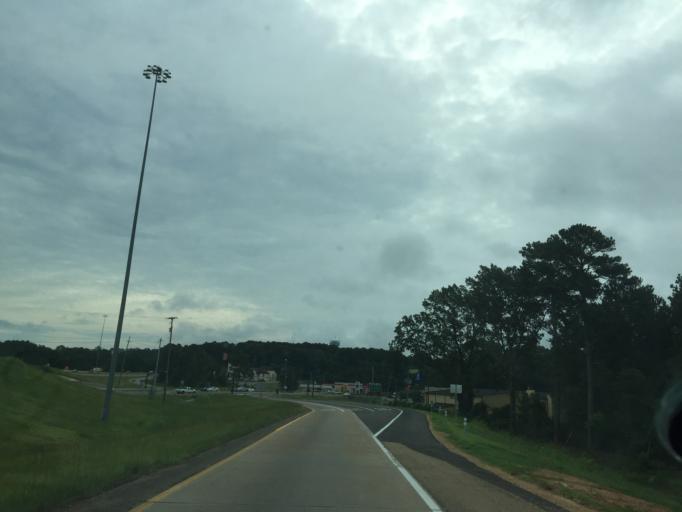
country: US
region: Mississippi
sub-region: Rankin County
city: Brandon
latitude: 32.2780
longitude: -90.0030
